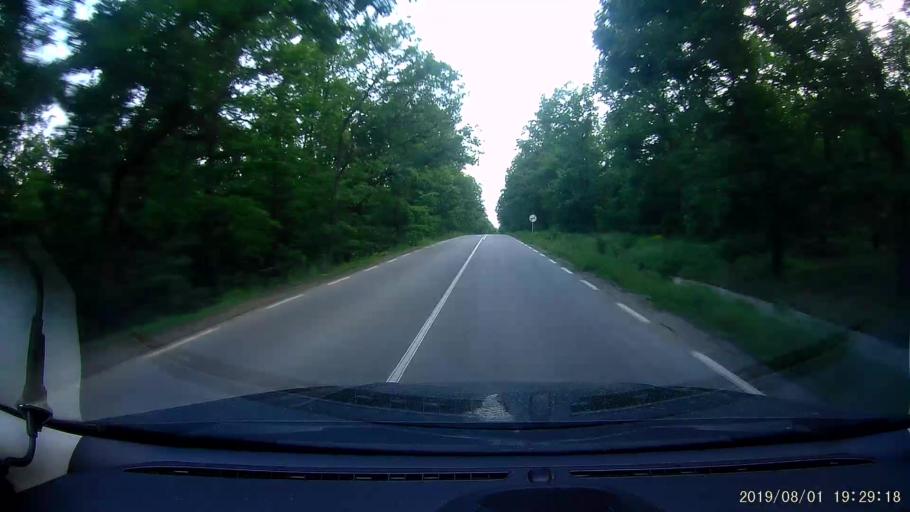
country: BG
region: Burgas
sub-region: Obshtina Sungurlare
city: Sungurlare
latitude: 42.8280
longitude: 26.9087
